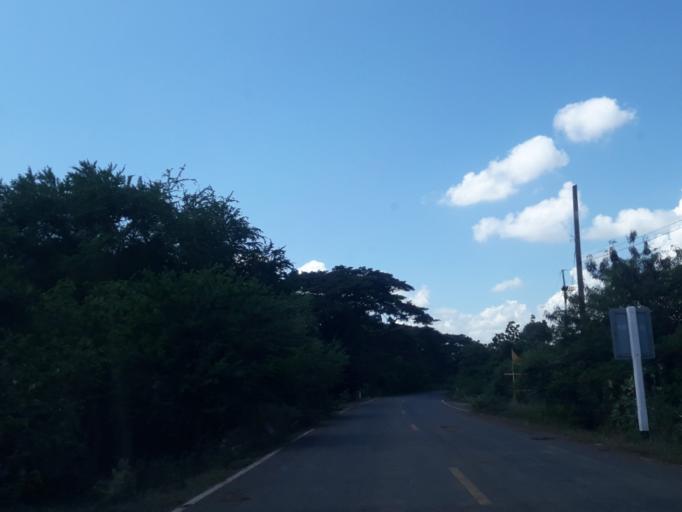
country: TH
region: Lop Buri
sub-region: Amphoe Tha Luang
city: Tha Luang
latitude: 15.0526
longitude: 101.0271
